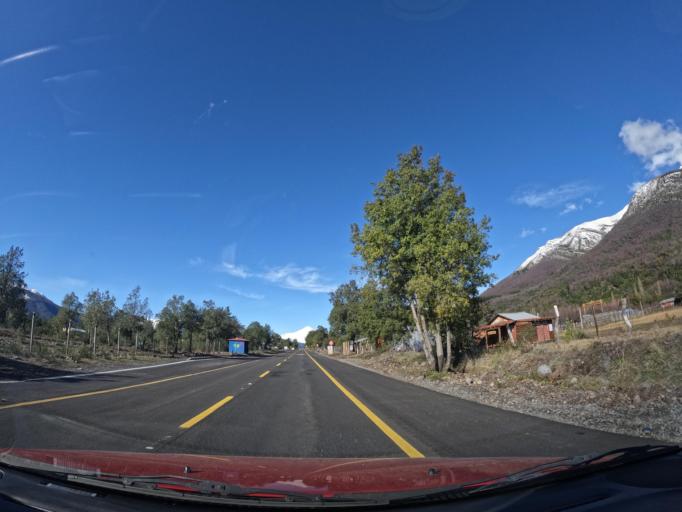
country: CL
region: Biobio
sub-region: Provincia de Biobio
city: Mulchen
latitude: -37.3348
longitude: -71.6215
